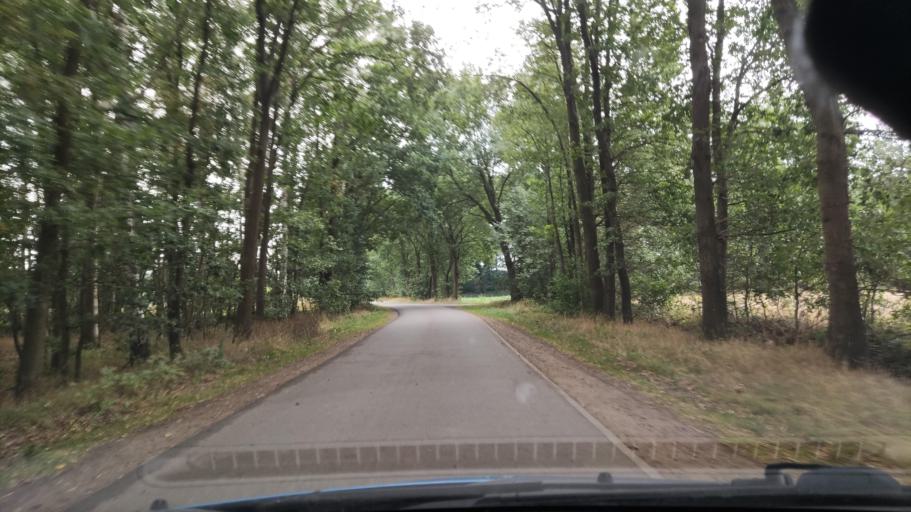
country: DE
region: Lower Saxony
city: Wittorf
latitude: 53.3458
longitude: 10.3733
